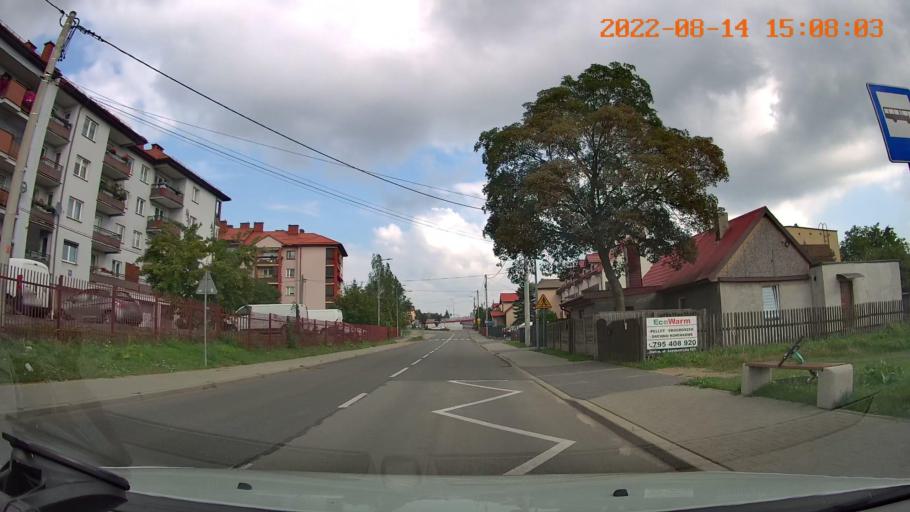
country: PL
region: Swietokrzyskie
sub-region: Powiat kielecki
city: Kielce
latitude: 50.8782
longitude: 20.5887
